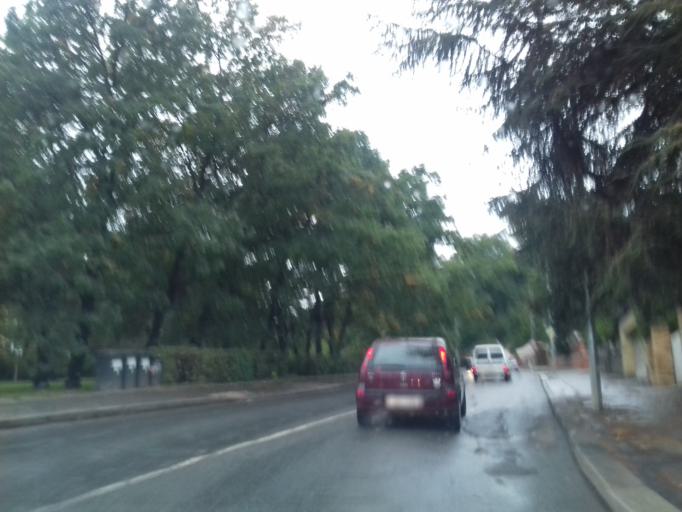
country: CZ
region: Praha
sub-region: Praha 1
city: Mala Strana
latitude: 50.0565
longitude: 14.3677
